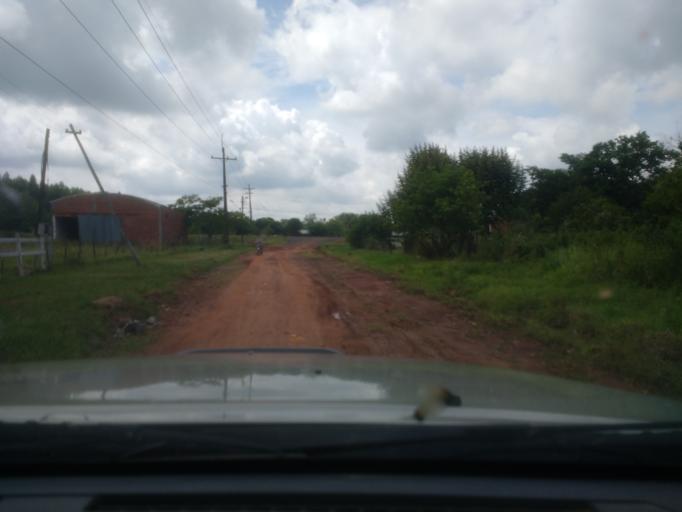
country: PY
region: San Pedro
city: Puerto Rosario
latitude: -24.4178
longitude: -57.1083
